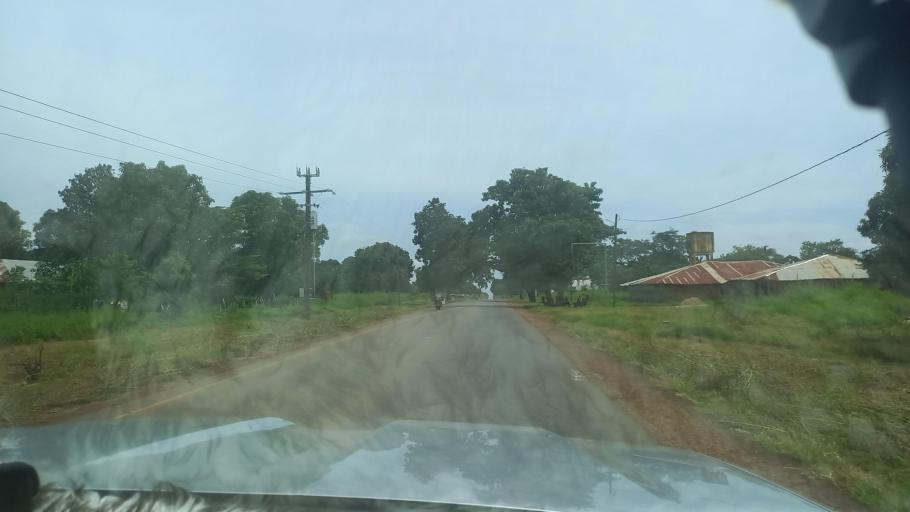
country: SN
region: Kolda
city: Marsassoum
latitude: 12.9609
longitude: -15.9907
